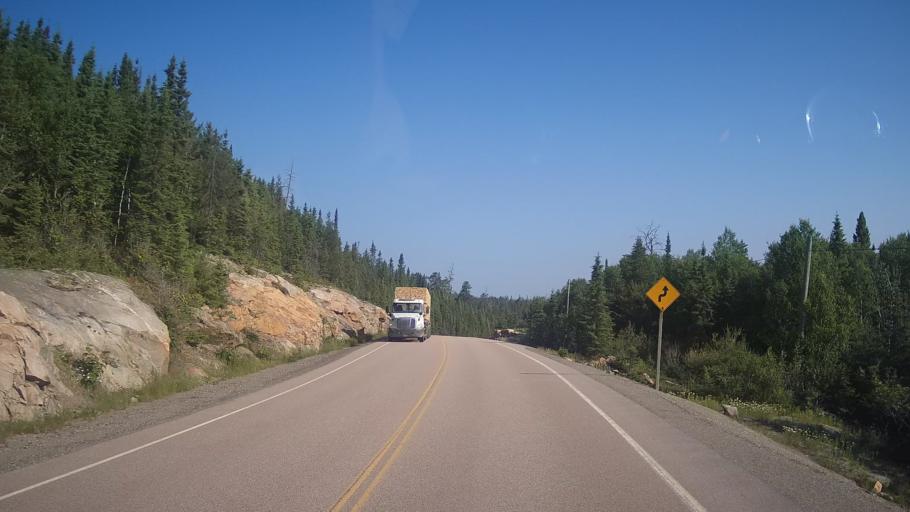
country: CA
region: Ontario
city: Rayside-Balfour
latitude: 47.0210
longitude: -81.6389
